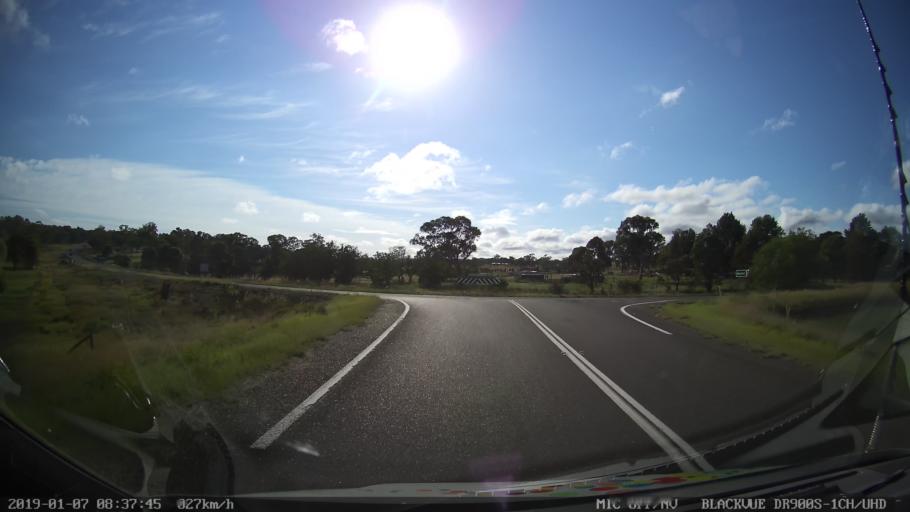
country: AU
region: New South Wales
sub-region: Tamworth Municipality
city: Kootingal
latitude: -30.8763
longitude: 151.1605
